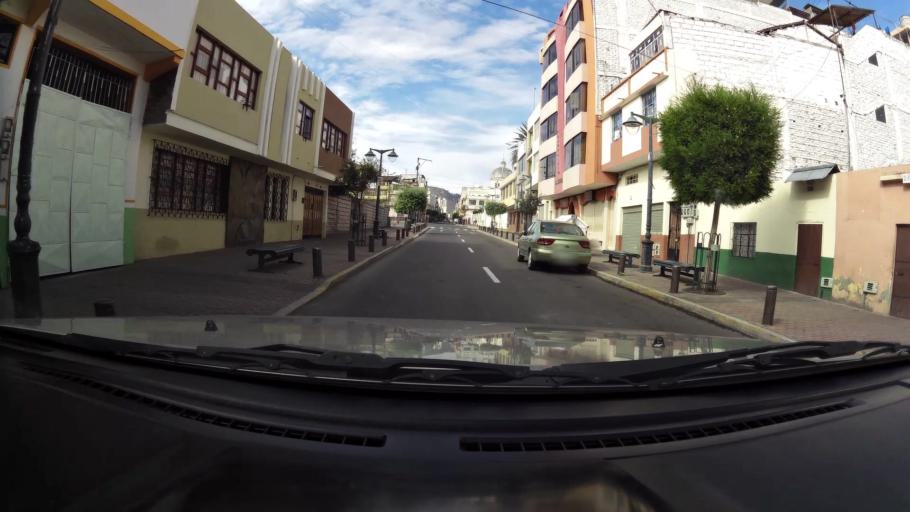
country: EC
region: Tungurahua
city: Ambato
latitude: -1.2349
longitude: -78.6269
